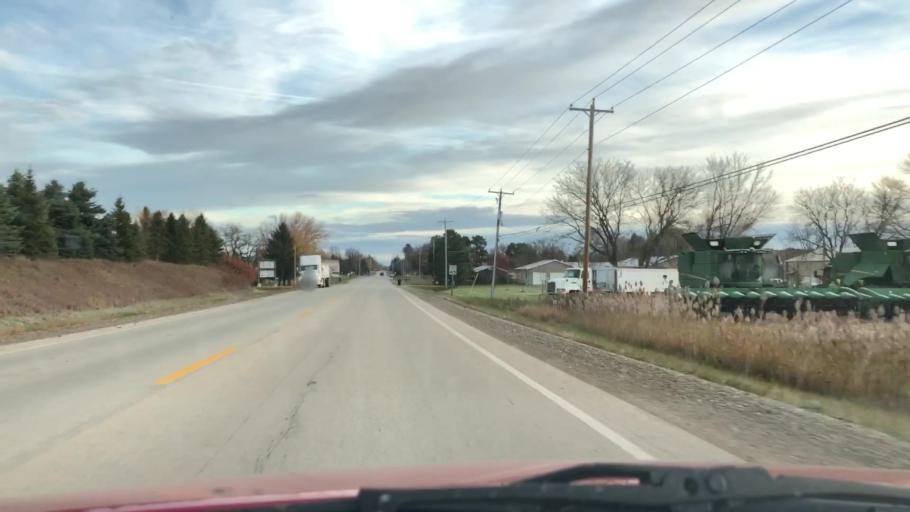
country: US
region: Wisconsin
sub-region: Brown County
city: Oneida
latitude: 44.4368
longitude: -88.2332
